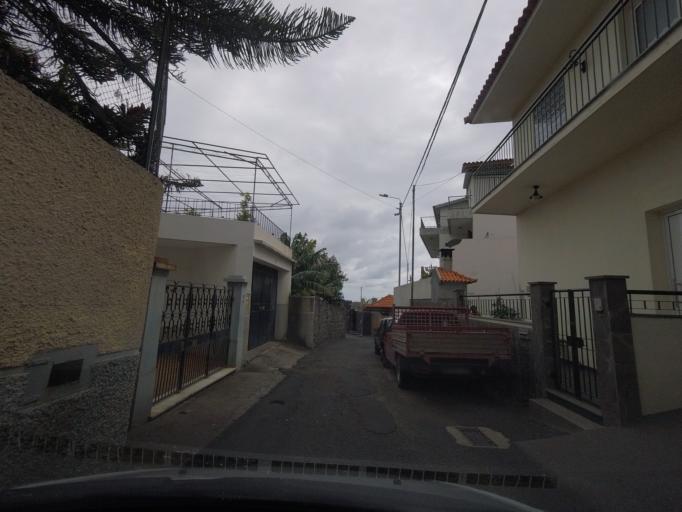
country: PT
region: Madeira
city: Camara de Lobos
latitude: 32.6500
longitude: -16.9696
